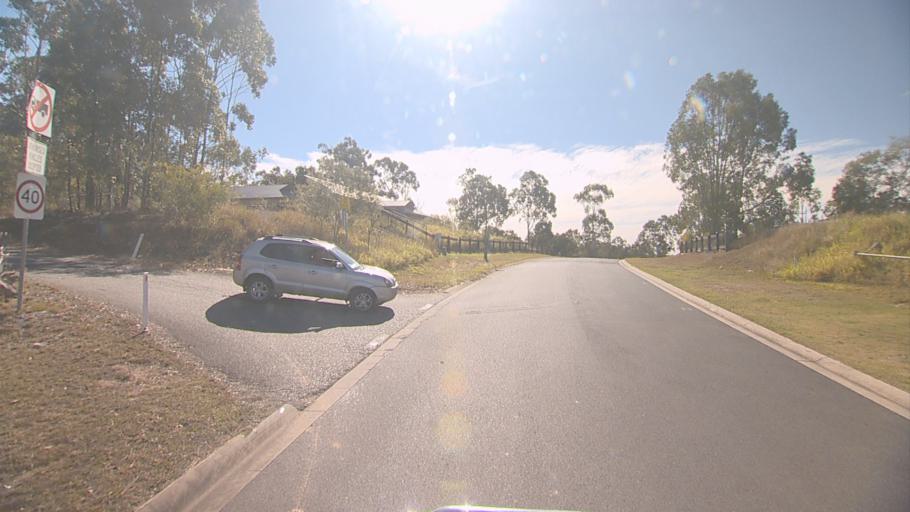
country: AU
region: Queensland
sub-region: Ipswich
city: Springfield Lakes
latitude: -27.7216
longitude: 152.9139
